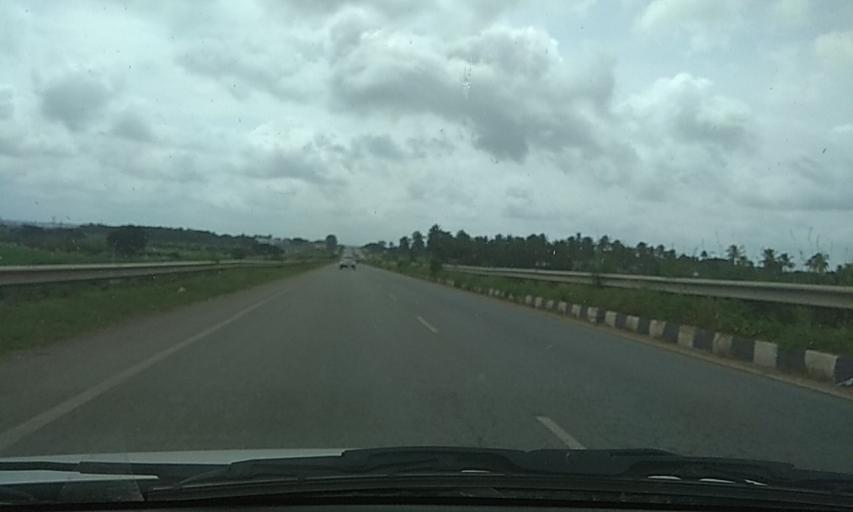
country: IN
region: Karnataka
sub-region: Davanagere
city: Harihar
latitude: 14.4586
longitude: 75.8600
